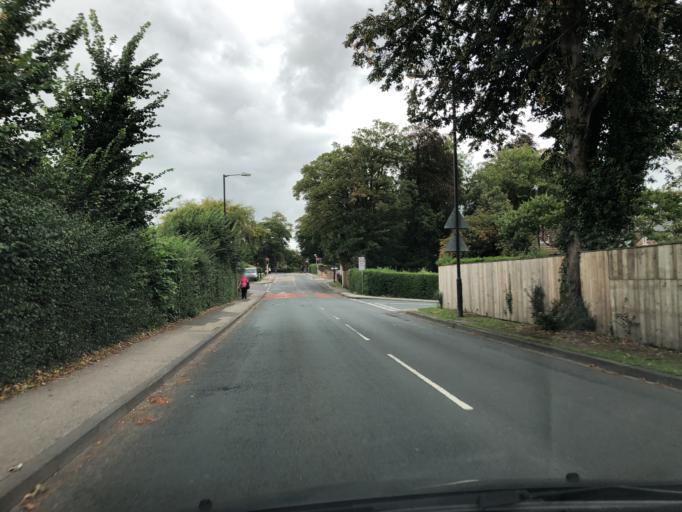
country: GB
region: England
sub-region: North Yorkshire
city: Ripon
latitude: 54.1257
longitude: -1.5263
